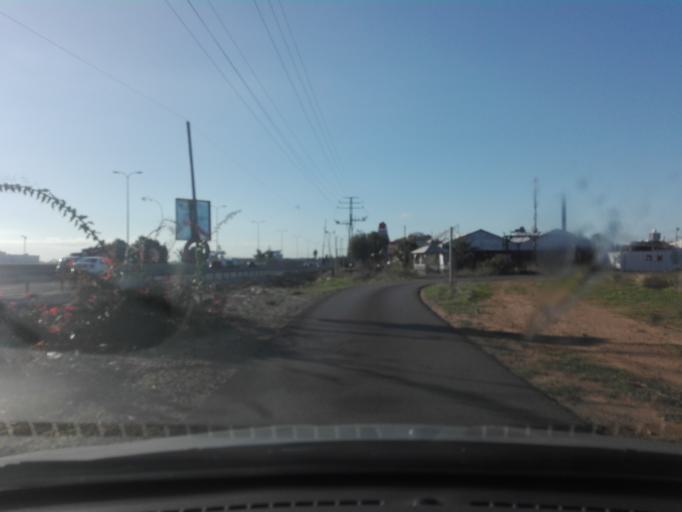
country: IL
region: Central District
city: Netanya
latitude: 32.3055
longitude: 34.8640
